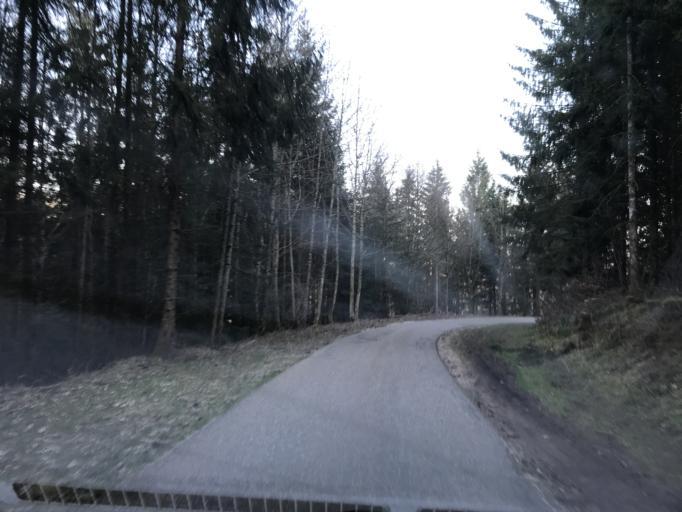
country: DE
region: Baden-Wuerttemberg
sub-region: Freiburg Region
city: Hausen
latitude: 47.6920
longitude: 7.8310
